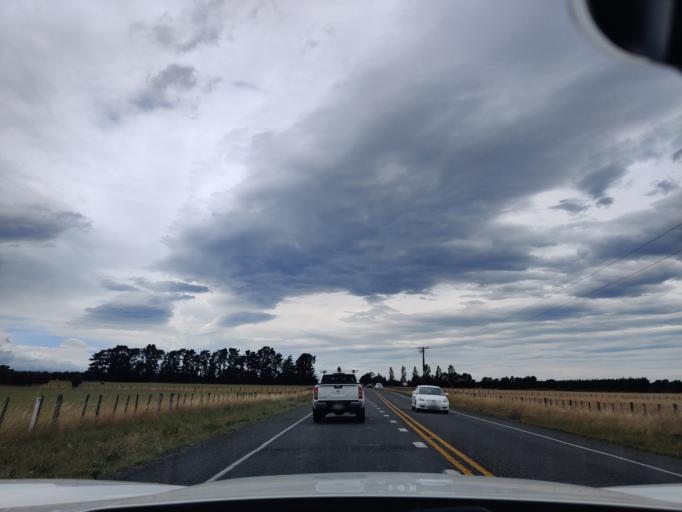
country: NZ
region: Wellington
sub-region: Masterton District
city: Masterton
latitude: -40.9980
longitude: 175.5596
